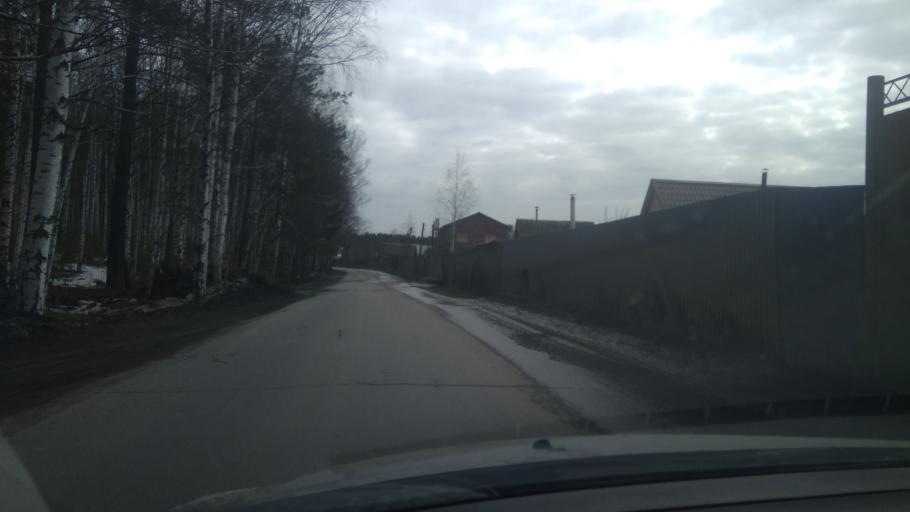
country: RU
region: Sverdlovsk
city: Severka
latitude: 56.8450
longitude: 60.3835
